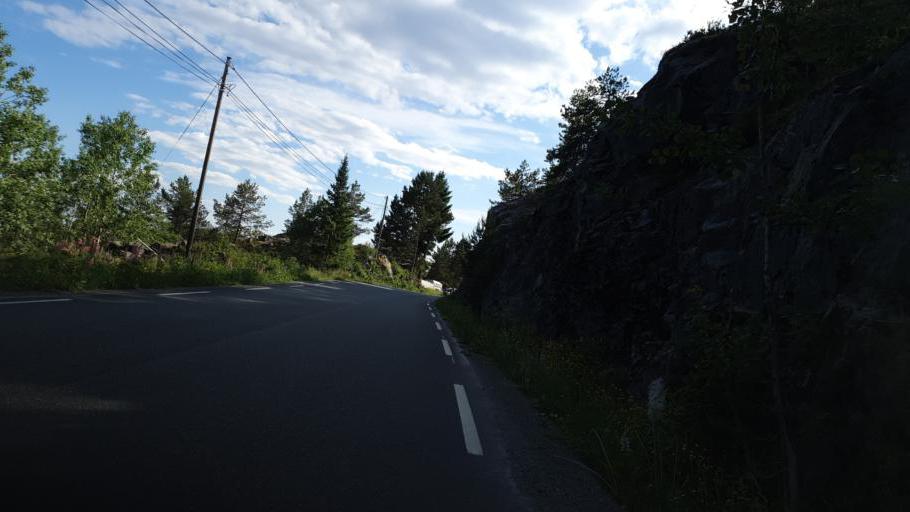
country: NO
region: Sor-Trondelag
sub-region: Trondheim
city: Trondheim
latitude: 63.5698
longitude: 10.3436
